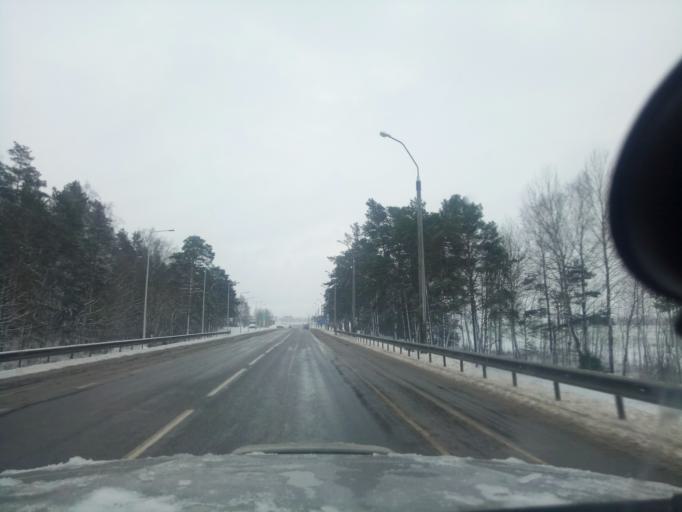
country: BY
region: Minsk
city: Nyasvizh
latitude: 53.2435
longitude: 26.6284
